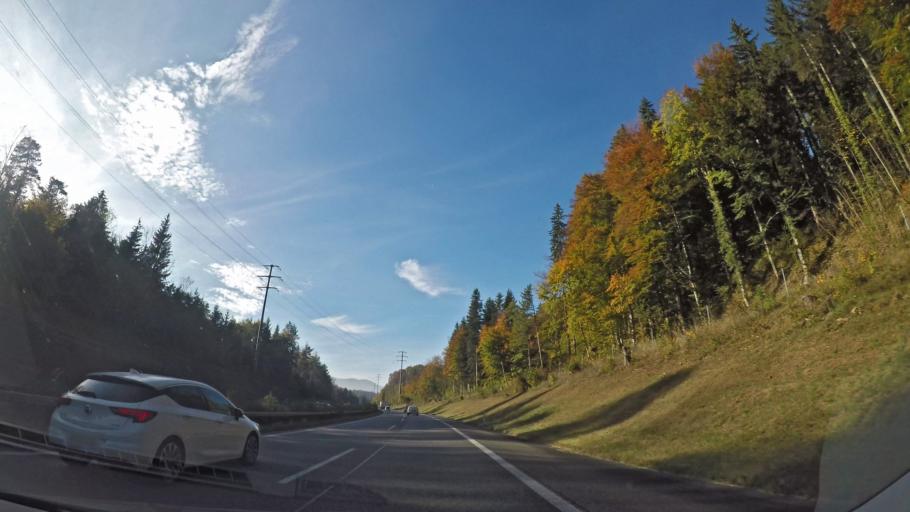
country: CH
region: Bern
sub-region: Frutigen-Niedersimmental District
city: Wimmis
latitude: 46.7116
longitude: 7.6289
